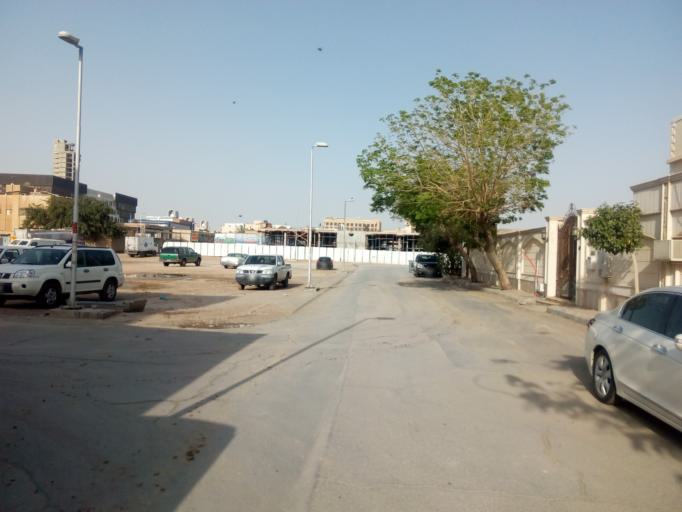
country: SA
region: Ar Riyad
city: Riyadh
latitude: 24.6501
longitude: 46.7076
